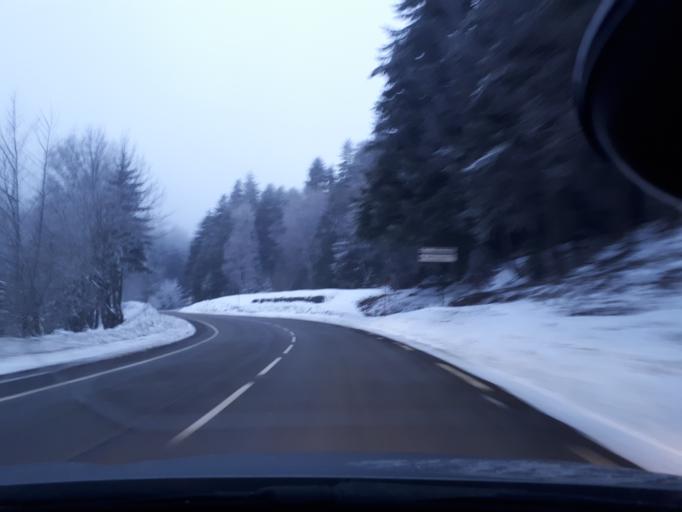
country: FR
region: Rhone-Alpes
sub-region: Departement de l'Isere
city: Vaulnaveys-le-Bas
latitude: 45.0915
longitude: 5.8500
